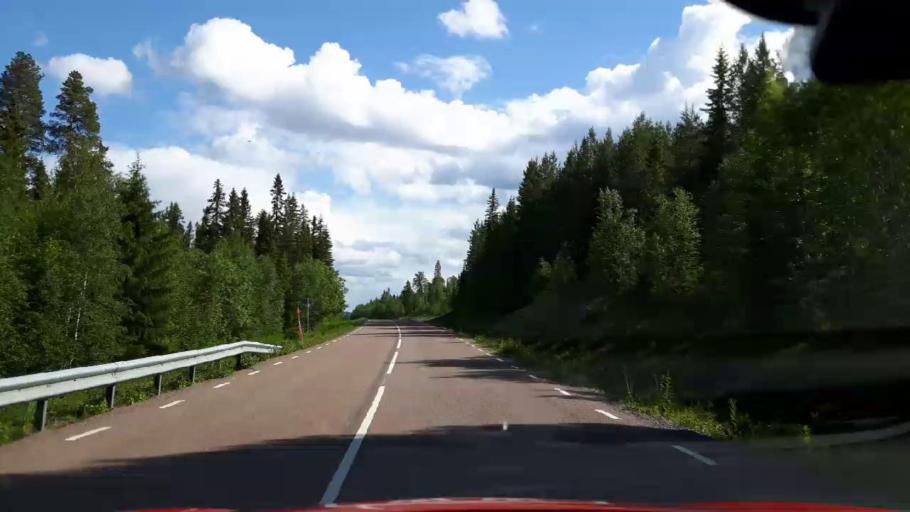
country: SE
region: Jaemtland
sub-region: Krokoms Kommun
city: Valla
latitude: 63.9973
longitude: 14.2318
